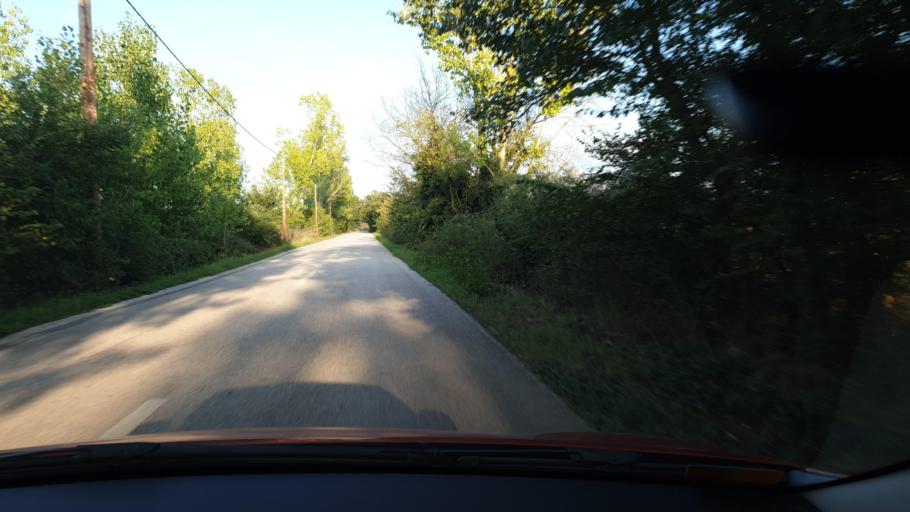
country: GR
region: Central Macedonia
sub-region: Nomos Chalkidikis
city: Galatista
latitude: 40.5643
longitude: 23.3290
